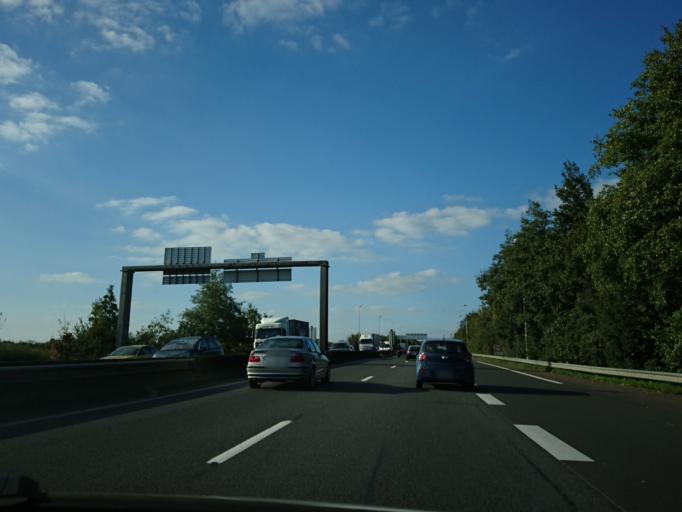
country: FR
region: Pays de la Loire
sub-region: Departement de la Loire-Atlantique
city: Bouguenais
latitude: 47.2024
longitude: -1.6225
